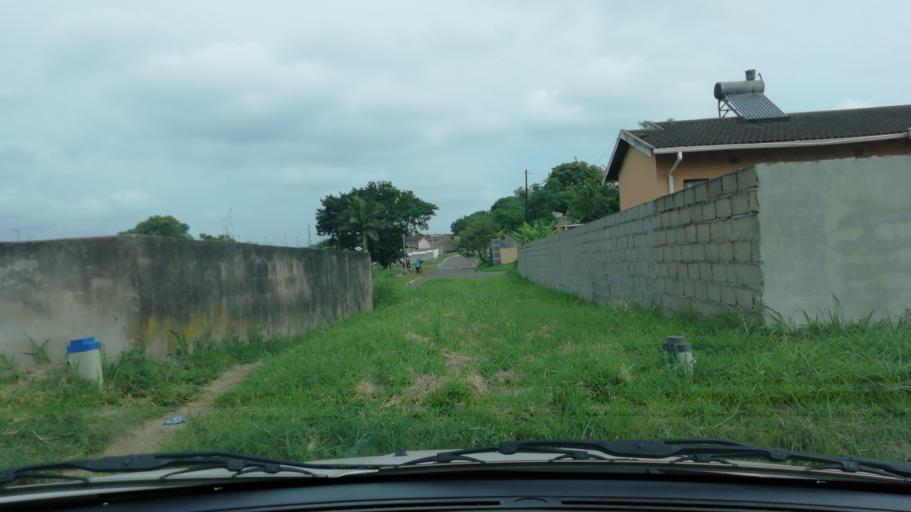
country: ZA
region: KwaZulu-Natal
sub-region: uThungulu District Municipality
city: Empangeni
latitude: -28.7360
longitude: 31.8776
